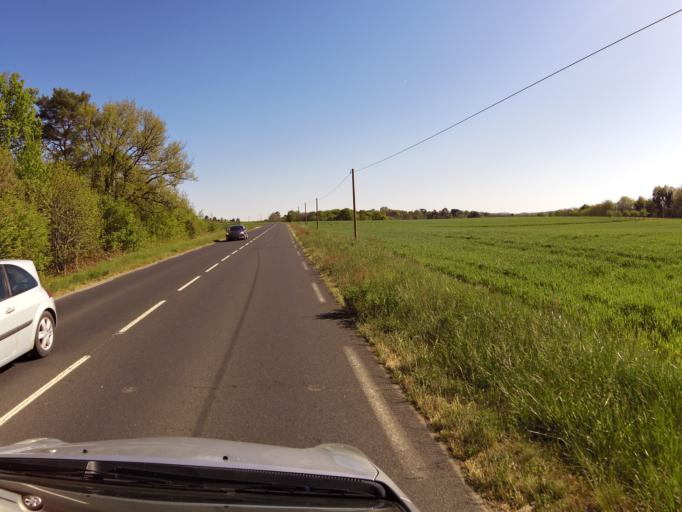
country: FR
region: Aquitaine
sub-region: Departement de la Dordogne
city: Montignac
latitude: 45.0288
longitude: 1.2287
